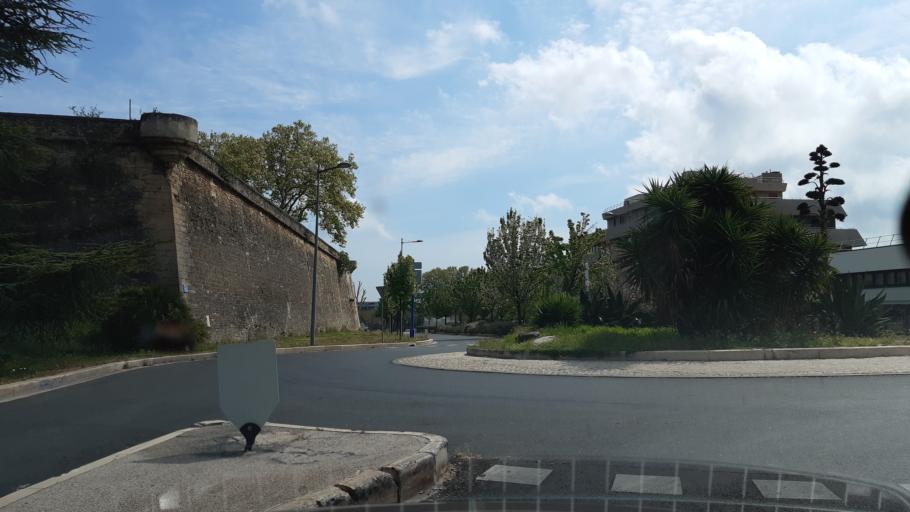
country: FR
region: Languedoc-Roussillon
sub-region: Departement de l'Herault
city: Montpellier
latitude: 43.6105
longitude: 3.8856
